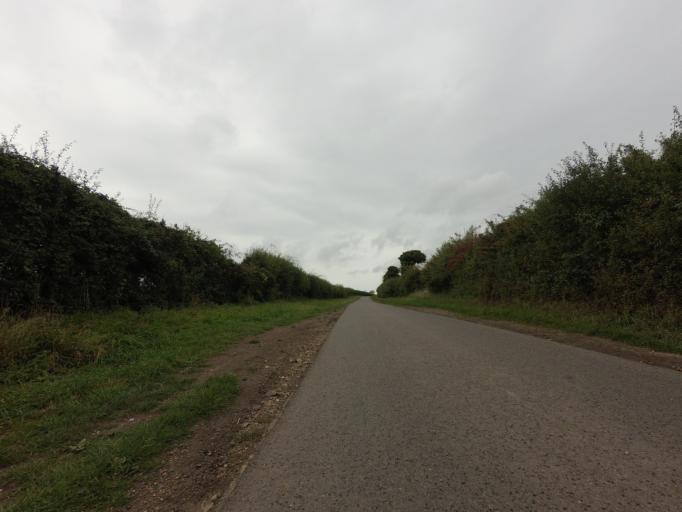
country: GB
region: England
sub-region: Cambridgeshire
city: Duxford
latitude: 52.0489
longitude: 0.1385
